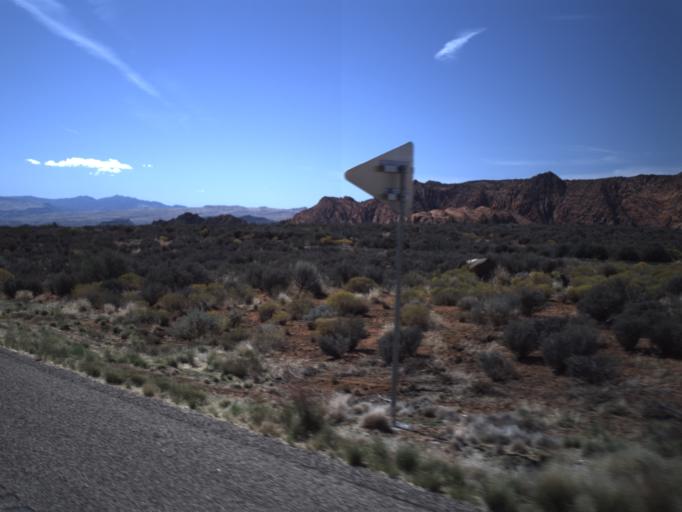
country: US
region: Utah
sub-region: Washington County
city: Ivins
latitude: 37.2242
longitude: -113.6335
